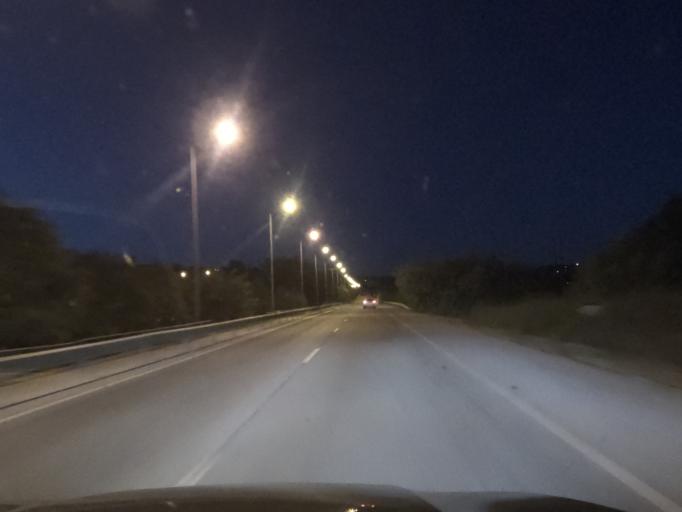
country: PT
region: Faro
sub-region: Loule
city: Loule
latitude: 37.1333
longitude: -8.0007
